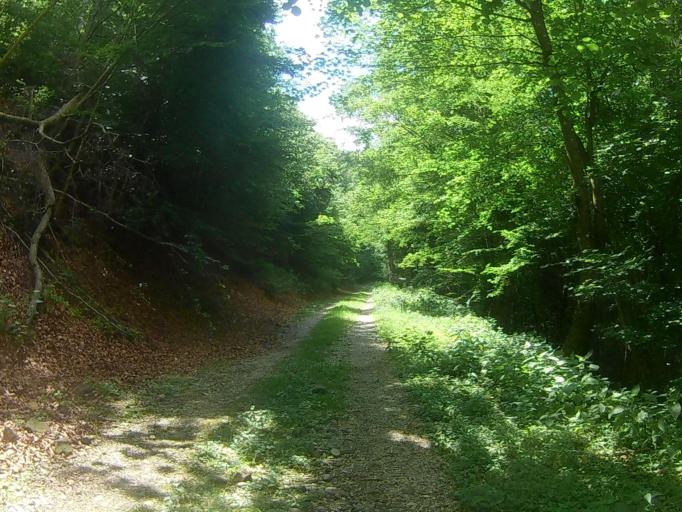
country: SI
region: Selnica ob Dravi
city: Selnica ob Dravi
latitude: 46.5208
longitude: 15.4896
